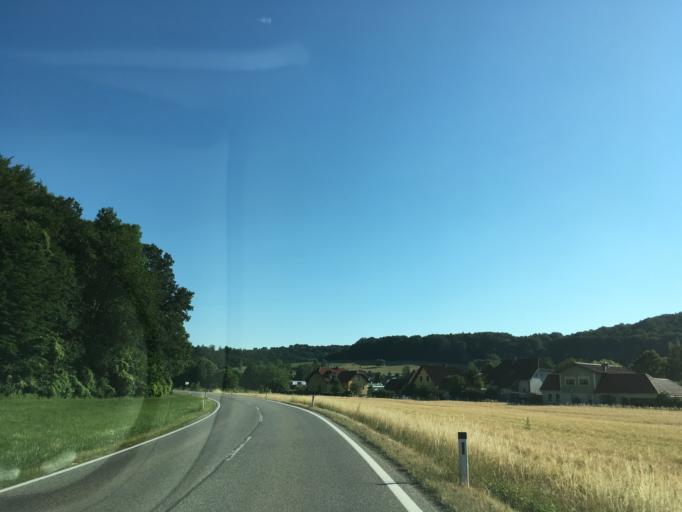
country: AT
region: Lower Austria
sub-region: Politischer Bezirk Sankt Polten
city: Boheimkirchen
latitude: 48.1718
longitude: 15.7537
